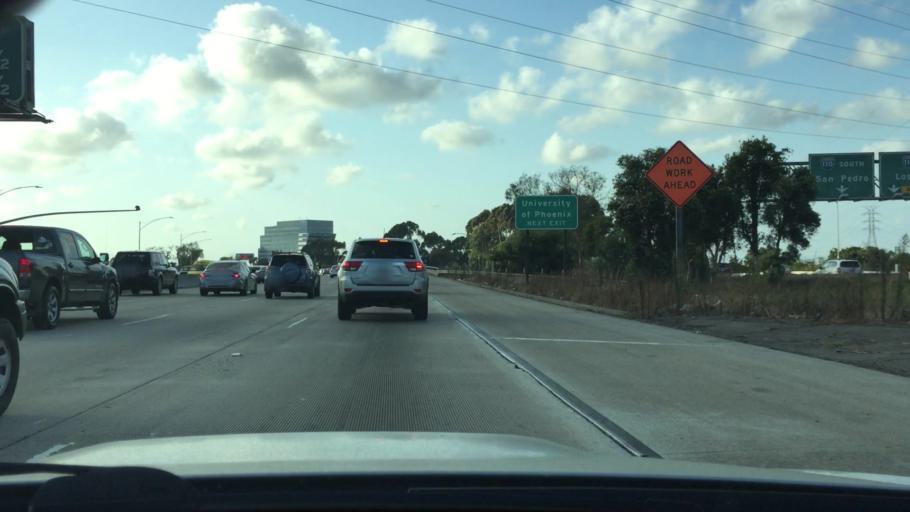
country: US
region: California
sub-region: Los Angeles County
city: Carson
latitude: 33.8553
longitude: -118.2821
